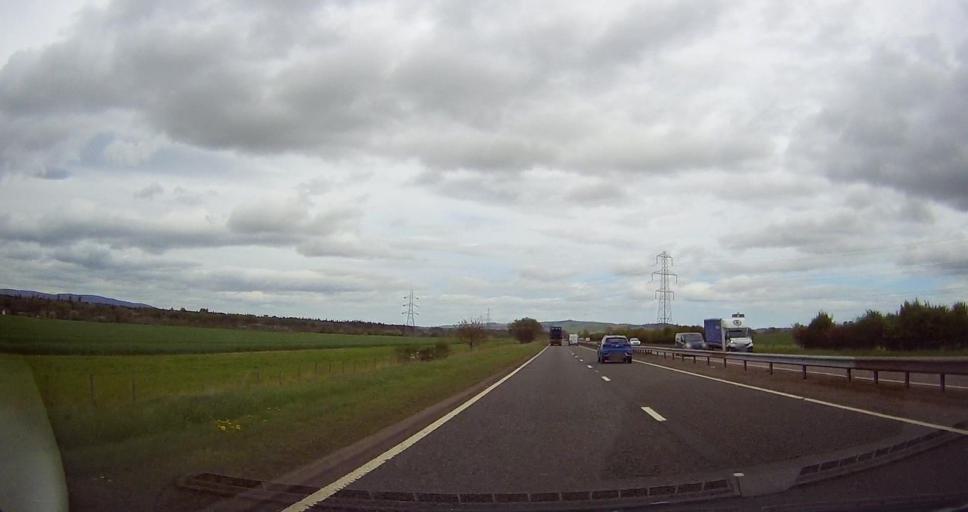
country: GB
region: Scotland
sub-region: Angus
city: Brechin
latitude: 56.7807
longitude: -2.5925
